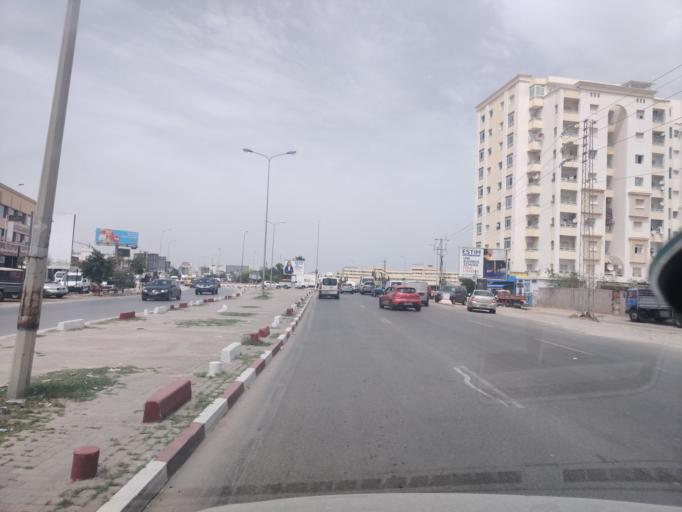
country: TN
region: Susah
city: Hammam Sousse
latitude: 35.8324
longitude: 10.5902
